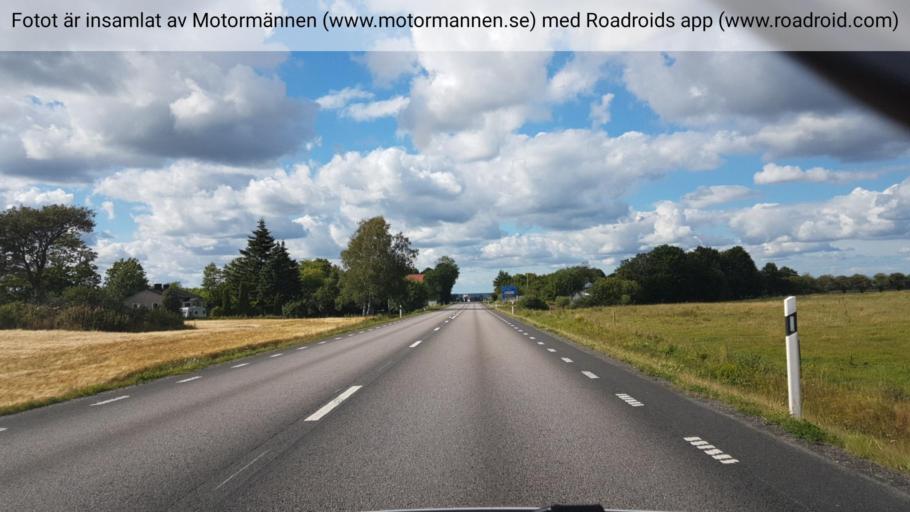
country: SE
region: Vaestra Goetaland
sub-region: Falkopings Kommun
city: Falkoeping
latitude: 58.2324
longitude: 13.5513
